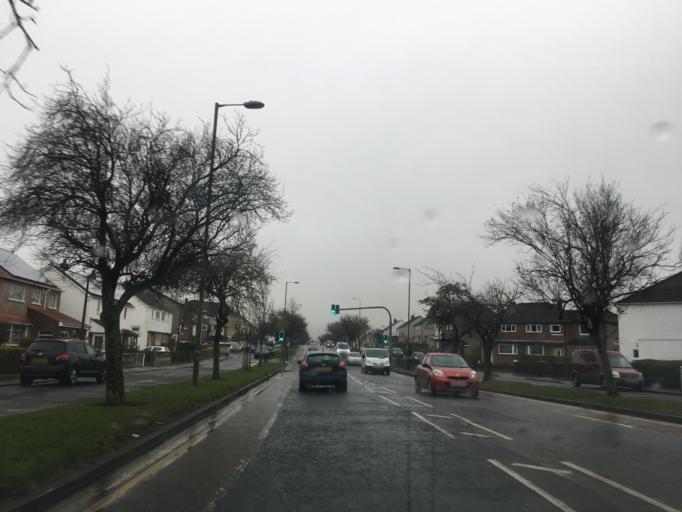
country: GB
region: Scotland
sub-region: Edinburgh
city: Currie
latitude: 55.9388
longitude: -3.2929
